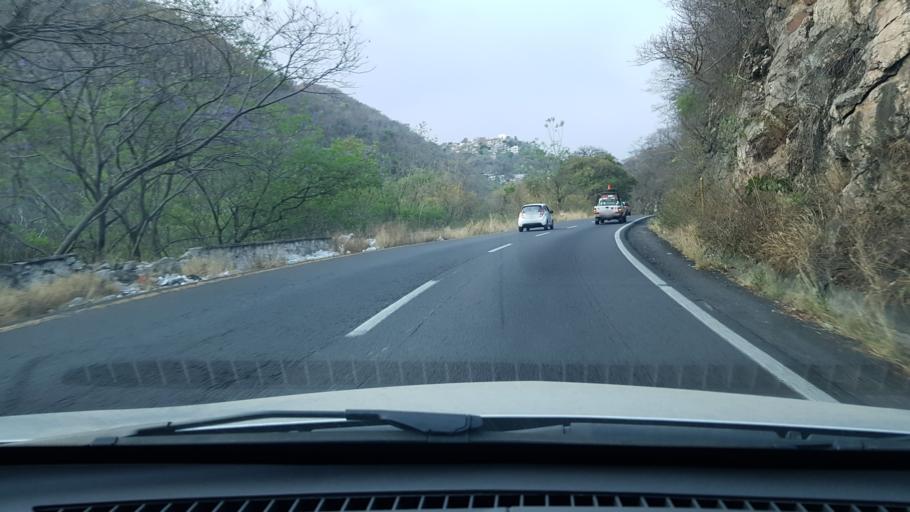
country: MX
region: Morelos
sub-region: Jiutepec
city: Independencia
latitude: 18.8707
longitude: -99.1196
